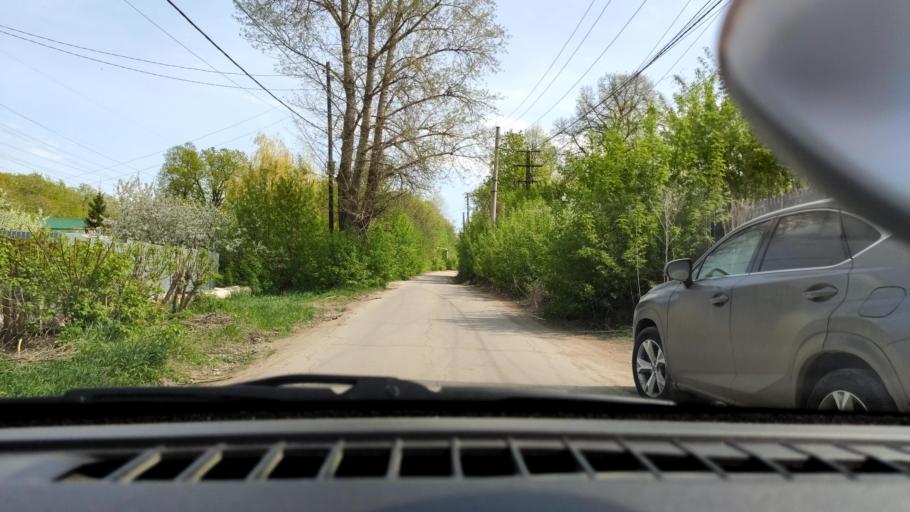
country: RU
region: Samara
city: Samara
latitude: 53.3040
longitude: 50.1983
